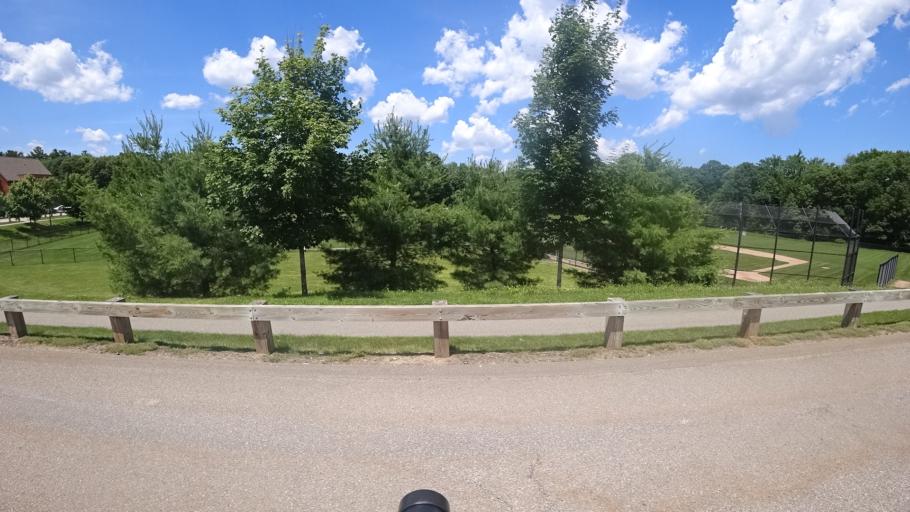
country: US
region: Massachusetts
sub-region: Norfolk County
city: Dedham
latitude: 42.2670
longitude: -71.1930
